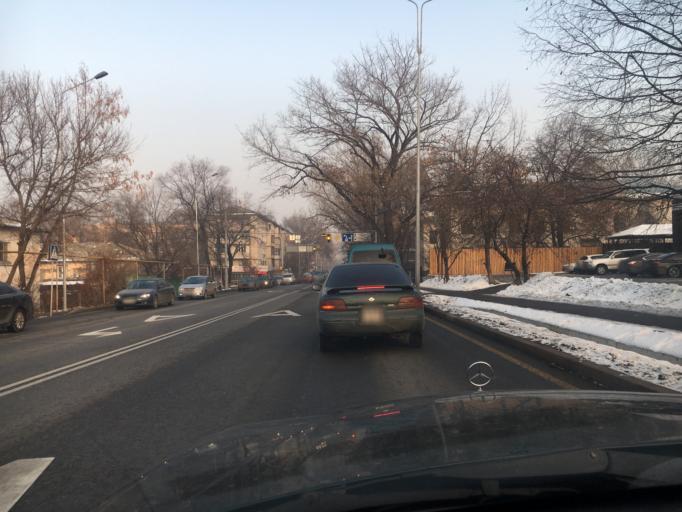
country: KZ
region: Almaty Qalasy
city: Almaty
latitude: 43.2063
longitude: 76.8784
